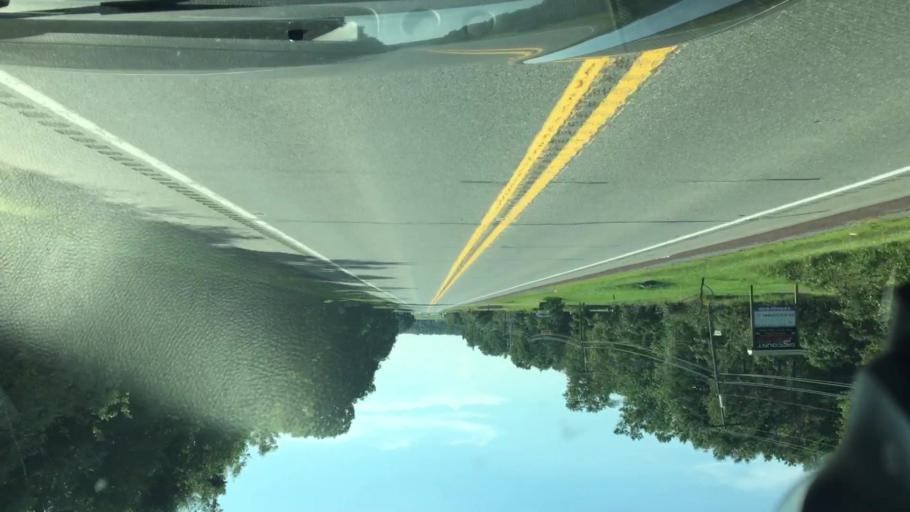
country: US
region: Pennsylvania
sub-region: Carbon County
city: Towamensing Trails
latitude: 40.9411
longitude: -75.6551
